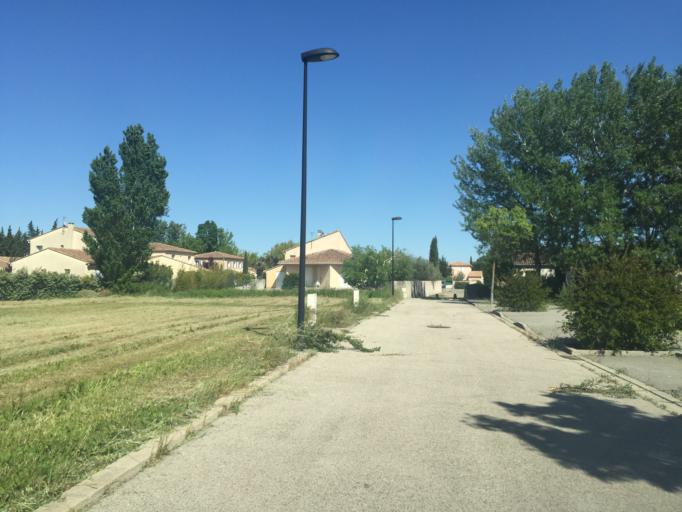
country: FR
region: Provence-Alpes-Cote d'Azur
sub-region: Departement du Vaucluse
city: Orange
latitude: 44.1423
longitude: 4.7912
